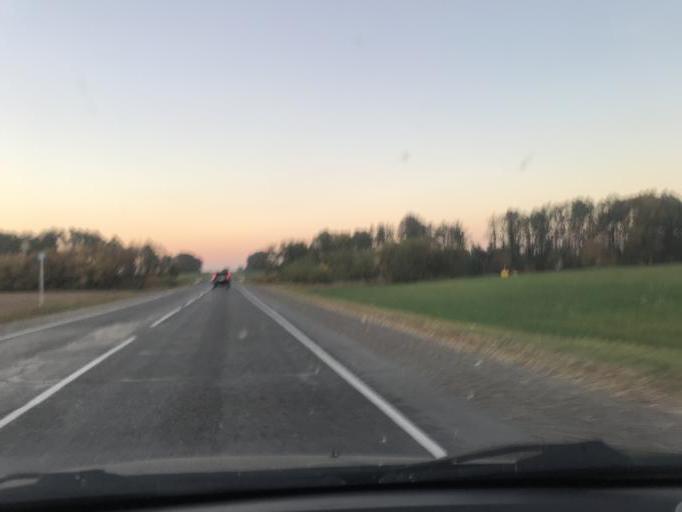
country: BY
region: Gomel
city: Horad Rechytsa
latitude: 52.2039
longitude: 30.5377
